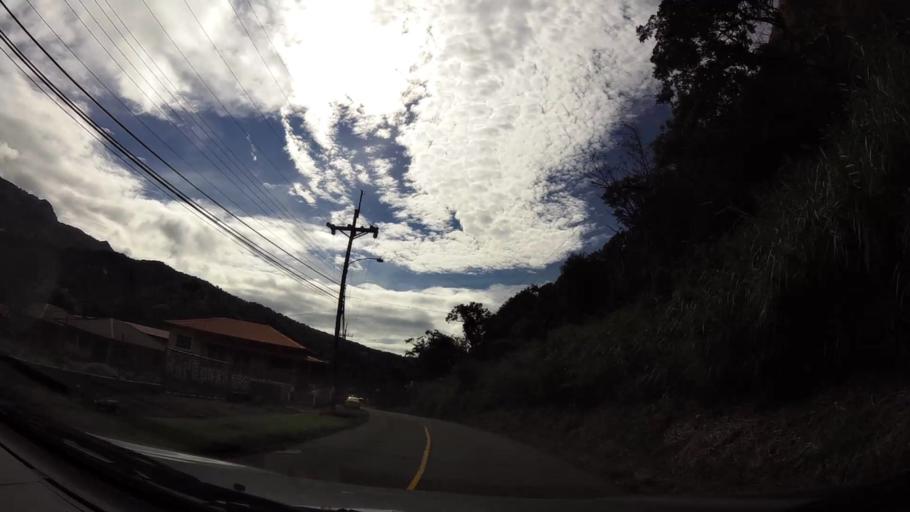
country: PA
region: Chiriqui
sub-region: Distrito Boquete
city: Boquete
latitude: 8.7835
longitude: -82.4343
